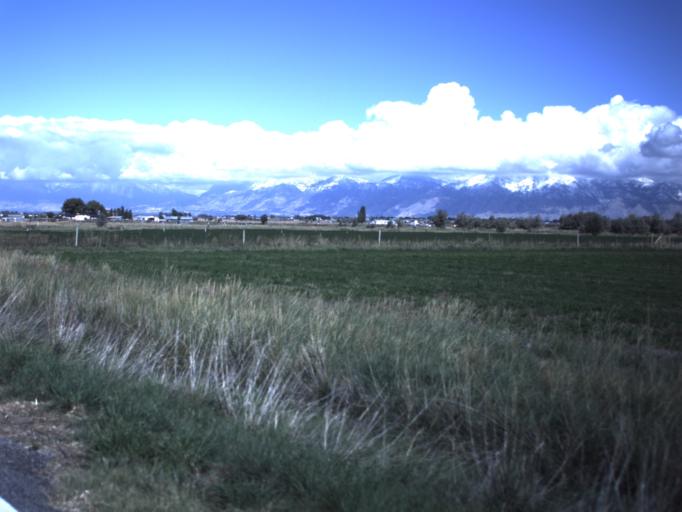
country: US
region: Utah
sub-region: Utah County
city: West Mountain
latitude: 40.0722
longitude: -111.7877
